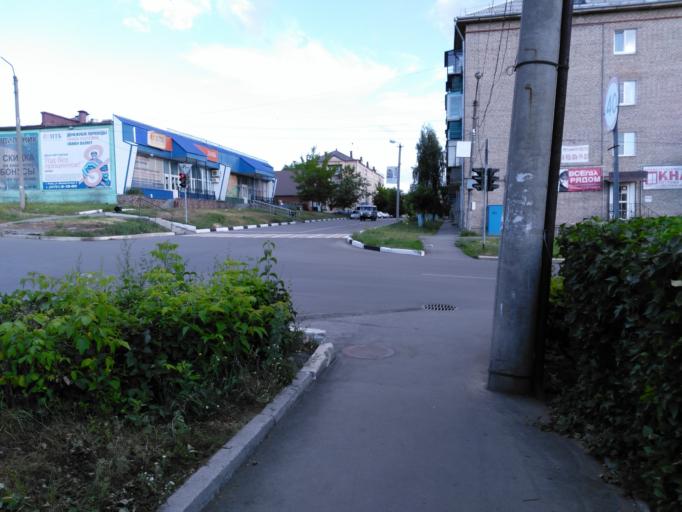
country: RU
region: Bashkortostan
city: Uchaly
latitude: 54.3174
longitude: 59.3837
